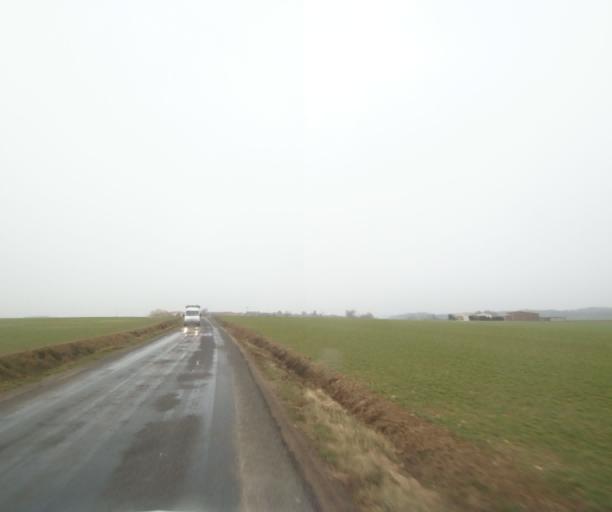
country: FR
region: Champagne-Ardenne
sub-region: Departement de la Haute-Marne
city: Bienville
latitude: 48.5253
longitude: 5.0419
